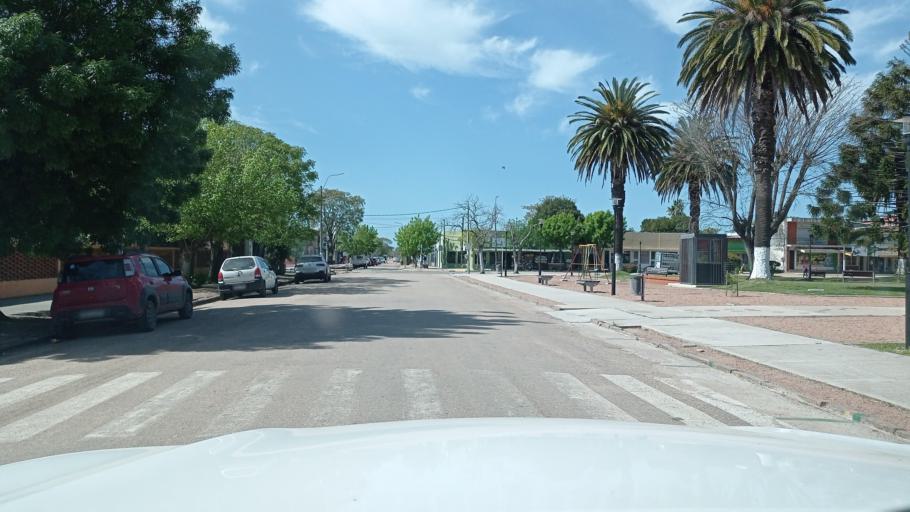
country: UY
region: Canelones
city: Santa Rosa
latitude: -34.4978
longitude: -56.0406
